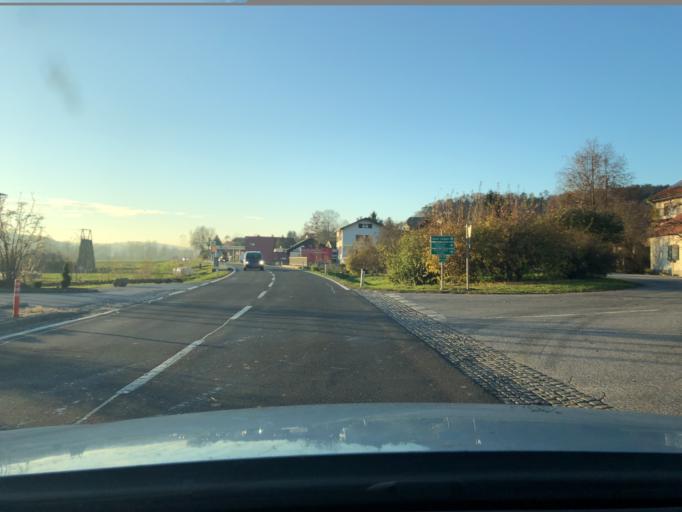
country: AT
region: Styria
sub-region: Politischer Bezirk Hartberg-Fuerstenfeld
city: Nestelbach im Ilztal
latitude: 47.0916
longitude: 15.8813
